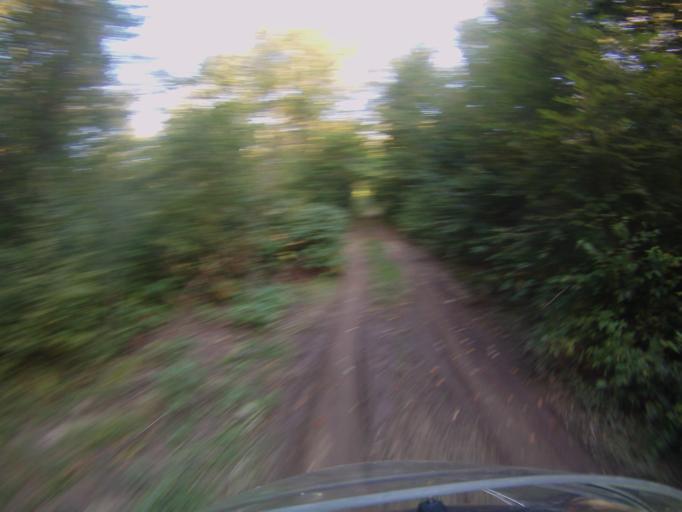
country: US
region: Vermont
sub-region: Addison County
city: Bristol
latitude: 44.0082
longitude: -73.0060
